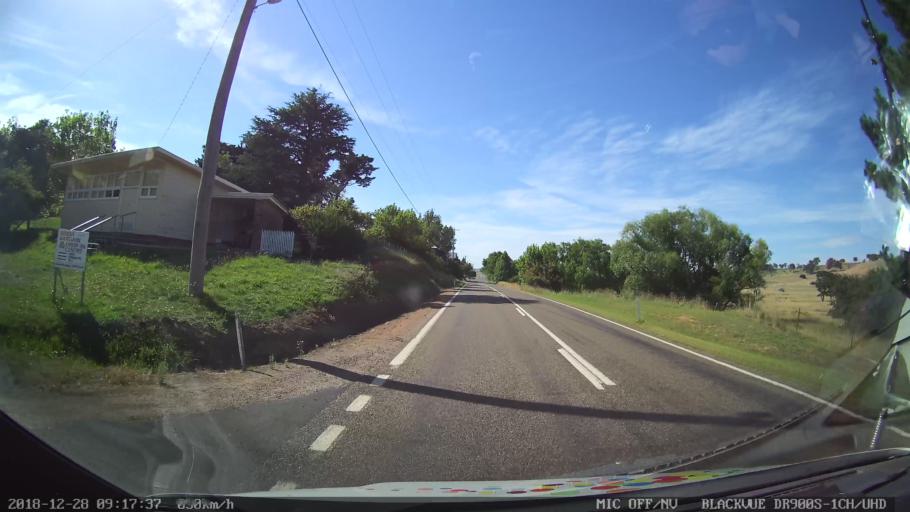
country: AU
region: New South Wales
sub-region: Upper Lachlan Shire
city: Crookwell
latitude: -34.3211
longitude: 149.3616
